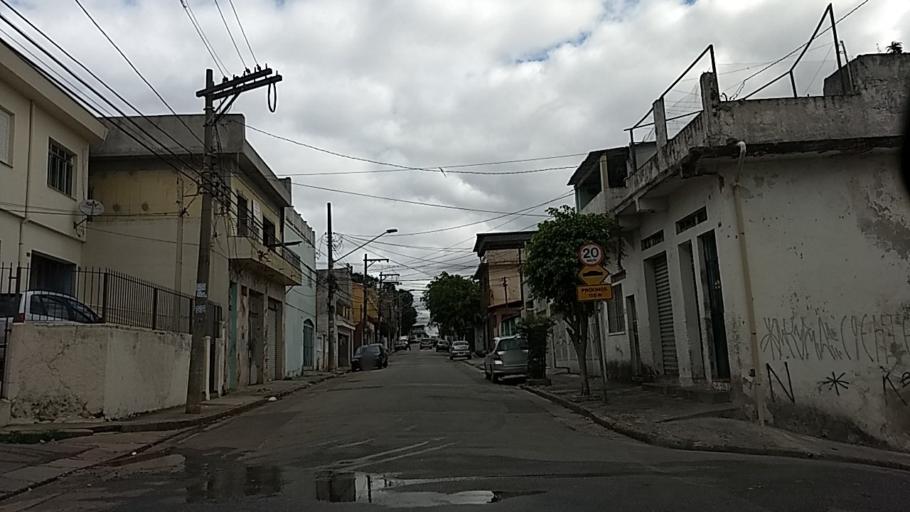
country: BR
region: Sao Paulo
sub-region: Guarulhos
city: Guarulhos
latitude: -23.4933
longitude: -46.5875
